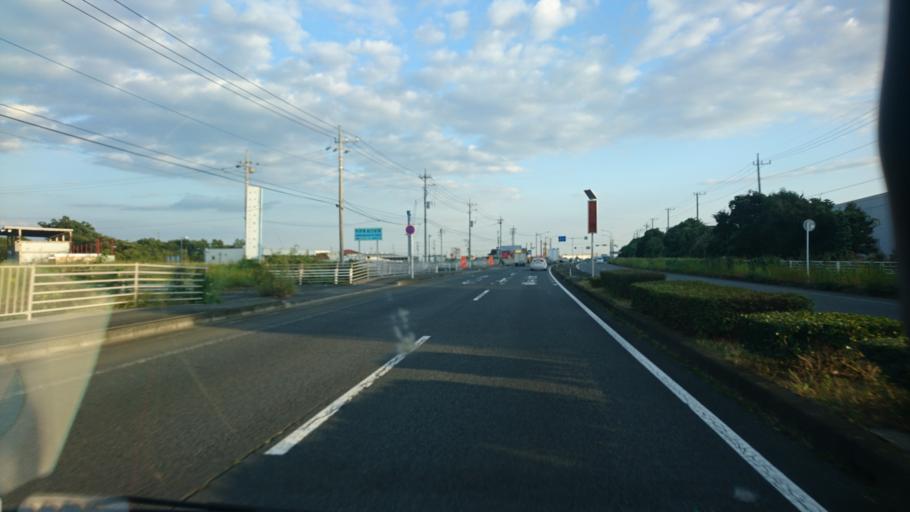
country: JP
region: Gunma
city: Kiryu
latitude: 36.3592
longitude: 139.3721
